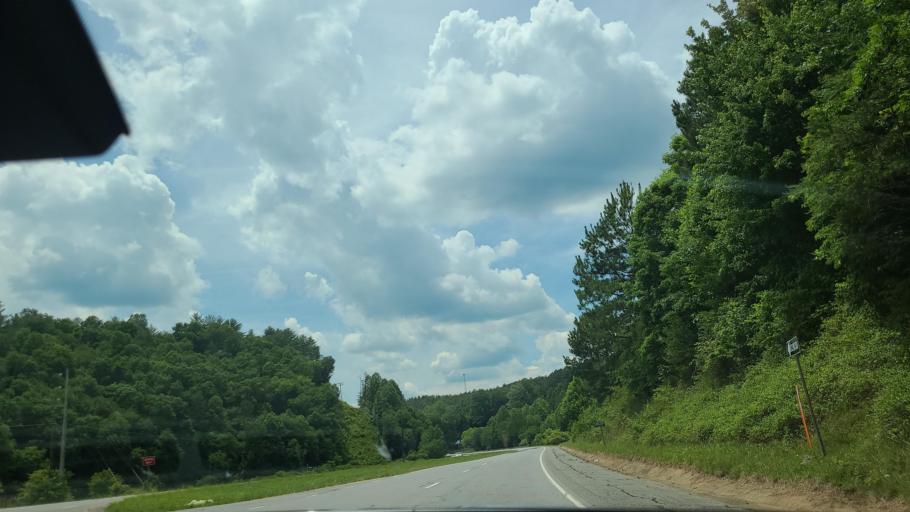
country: US
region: Georgia
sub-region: Fannin County
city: McCaysville
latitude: 35.0242
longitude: -84.2225
